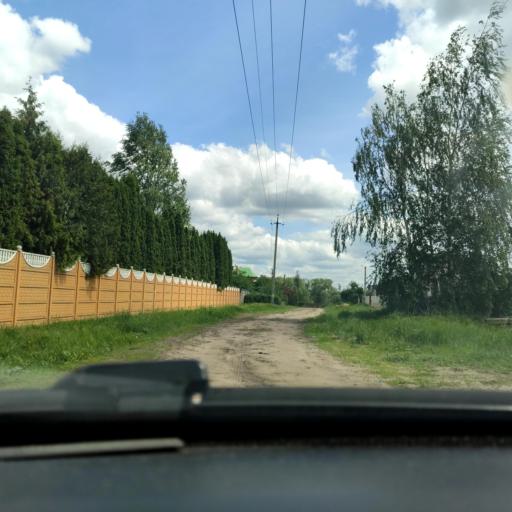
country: RU
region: Voronezj
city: Somovo
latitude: 51.6952
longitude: 39.3202
